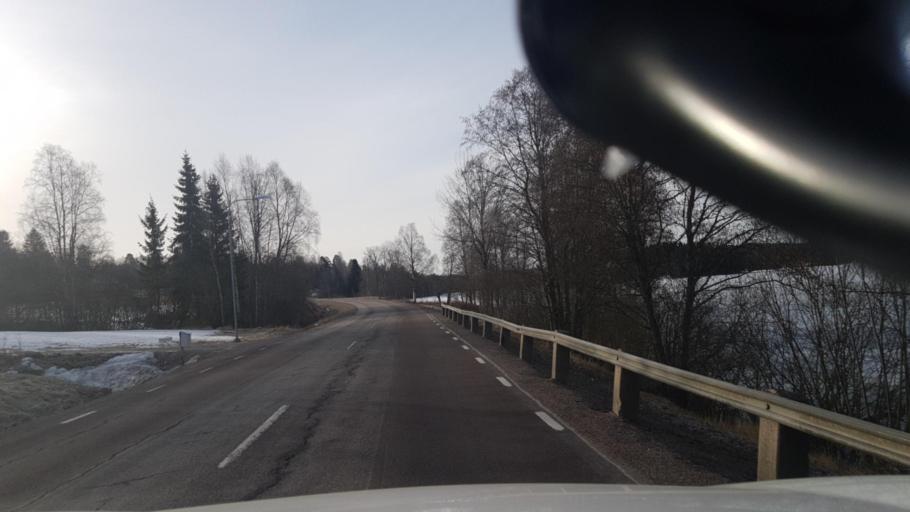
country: SE
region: Vaermland
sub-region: Eda Kommun
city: Amotfors
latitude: 59.8841
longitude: 12.5255
